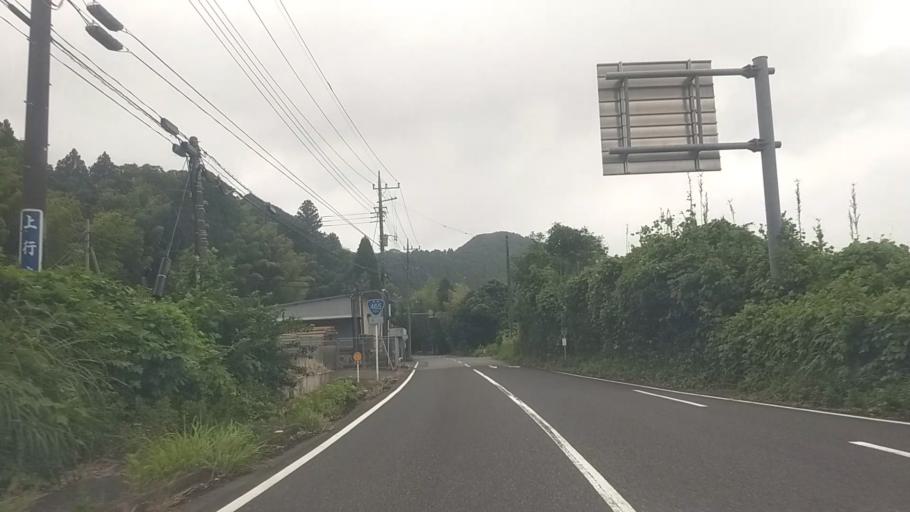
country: JP
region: Chiba
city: Katsuura
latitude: 35.2425
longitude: 140.2430
